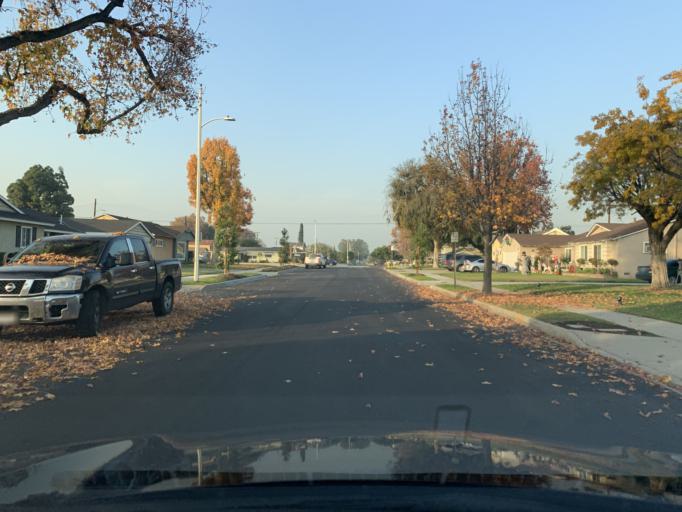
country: US
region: California
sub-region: Los Angeles County
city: Covina
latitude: 34.0855
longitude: -117.9012
